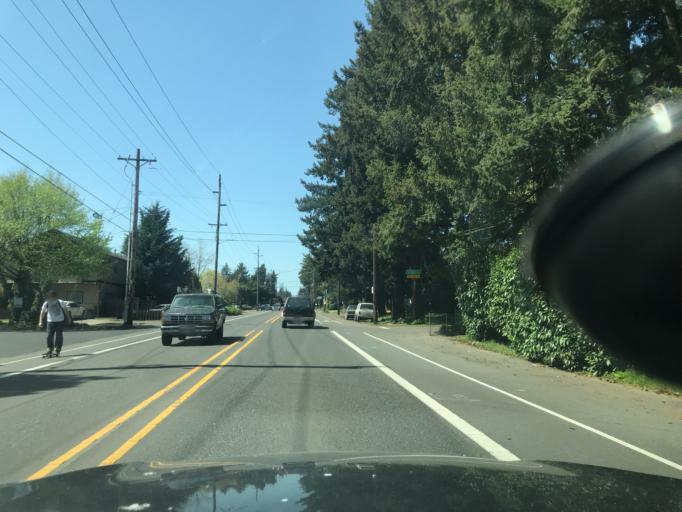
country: US
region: Oregon
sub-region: Multnomah County
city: Lents
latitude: 45.4975
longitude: -122.5280
